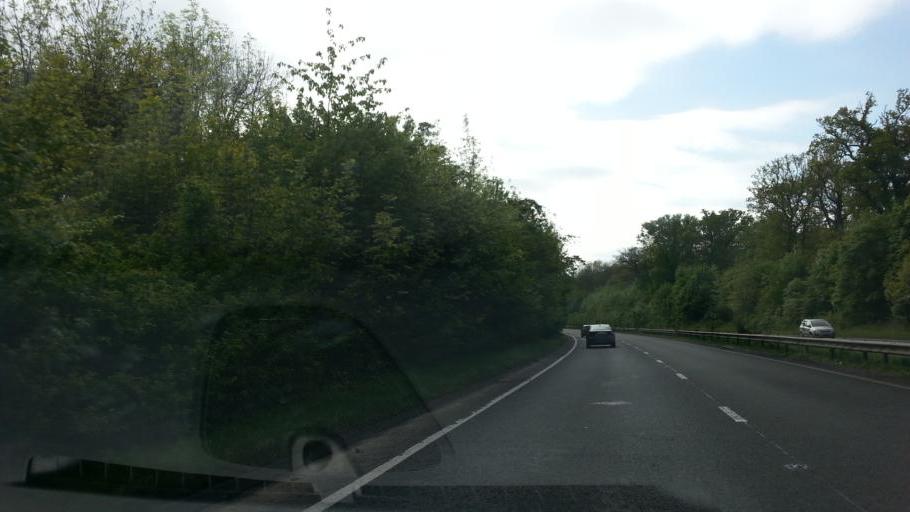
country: GB
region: England
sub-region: Peterborough
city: Marholm
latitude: 52.5726
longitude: -0.3071
